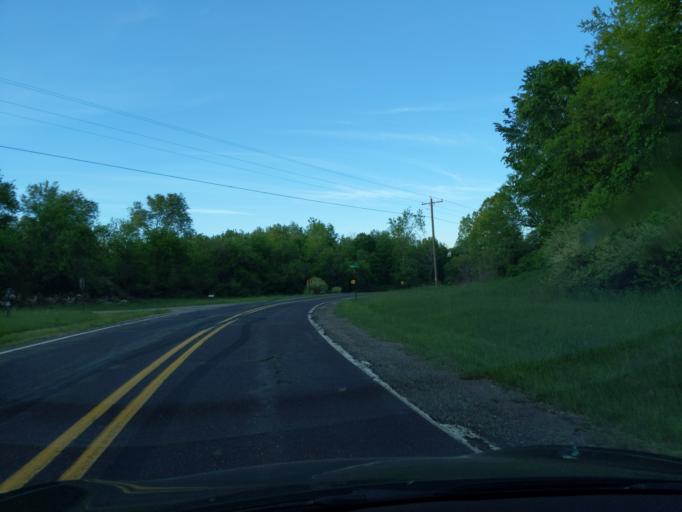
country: US
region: Michigan
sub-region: Ingham County
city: Leslie
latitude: 42.5094
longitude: -84.3119
